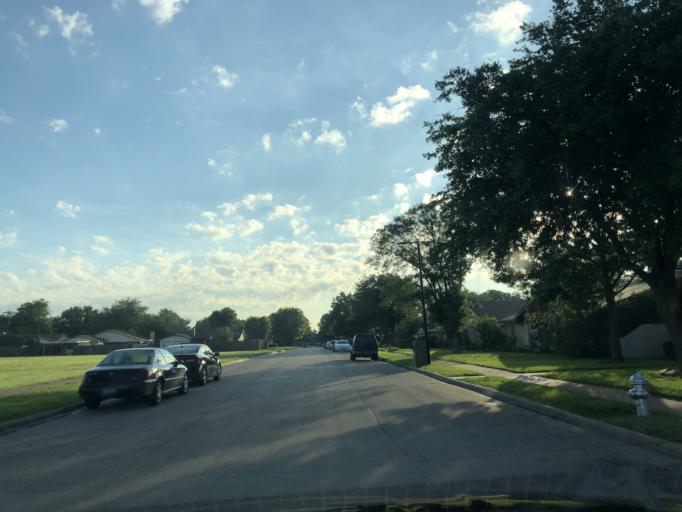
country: US
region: Texas
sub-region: Dallas County
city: Garland
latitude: 32.8468
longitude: -96.6231
